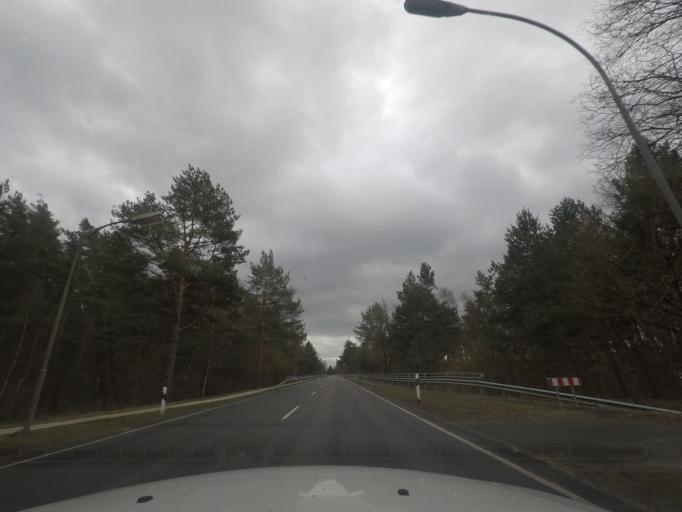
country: DE
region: Lower Saxony
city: Bad Bevensen
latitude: 53.0694
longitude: 10.5970
